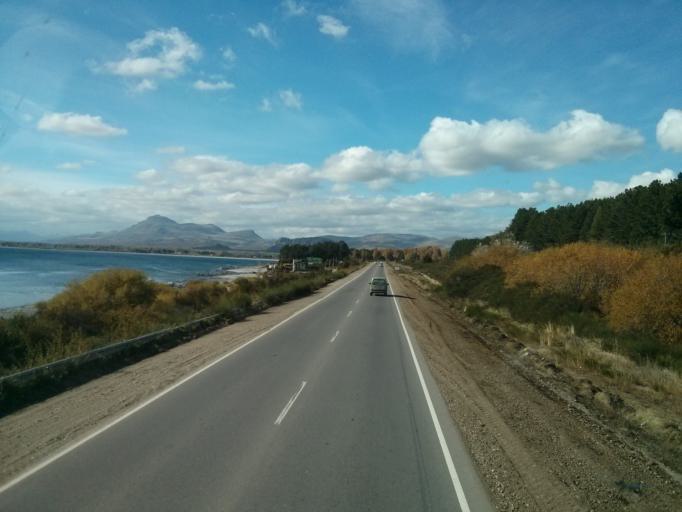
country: AR
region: Rio Negro
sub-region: Departamento de Bariloche
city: San Carlos de Bariloche
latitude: -41.1073
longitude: -71.2104
